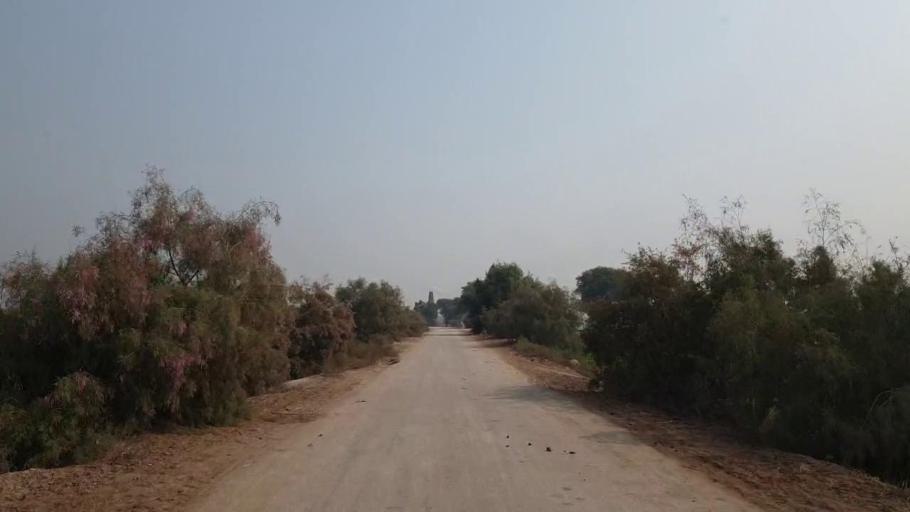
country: PK
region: Sindh
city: Bhan
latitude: 26.5166
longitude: 67.7233
